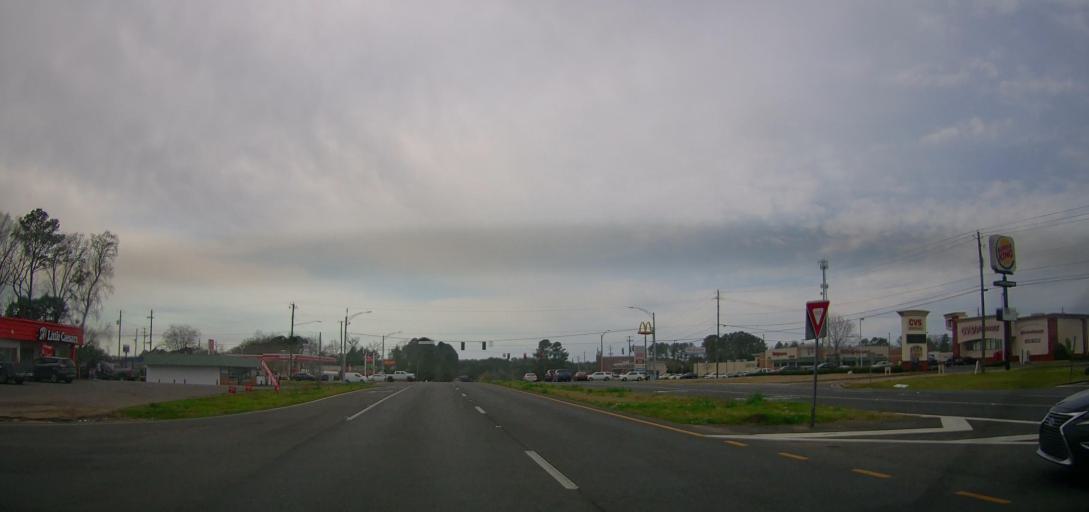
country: US
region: Alabama
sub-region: Walker County
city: Jasper
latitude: 33.8477
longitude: -87.2667
